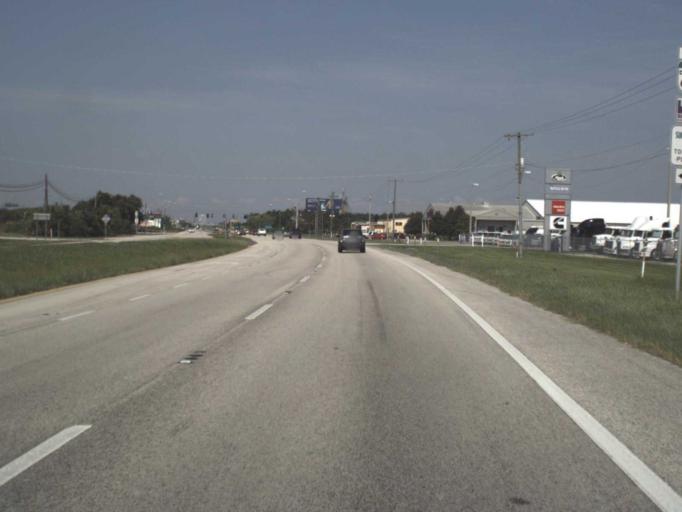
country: US
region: Florida
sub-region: Hillsborough County
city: Palm River-Clair Mel
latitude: 27.9523
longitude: -82.3657
